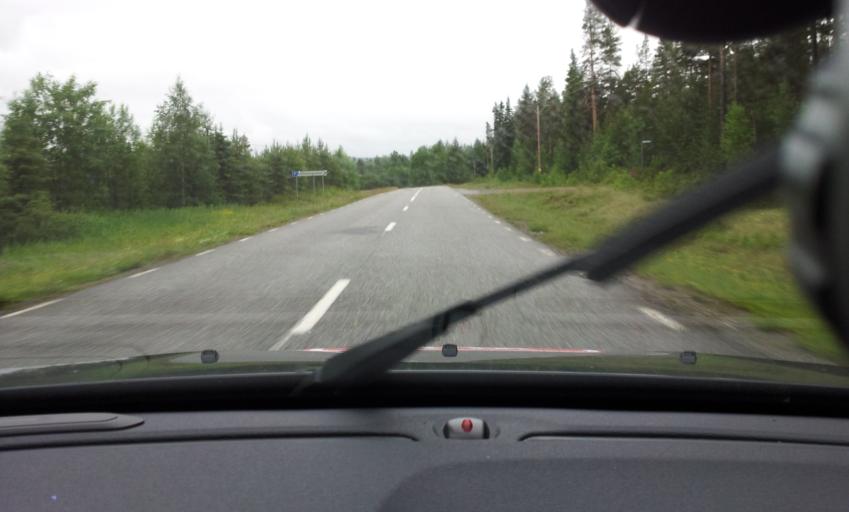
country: SE
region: Jaemtland
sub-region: Stroemsunds Kommun
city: Stroemsund
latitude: 63.3070
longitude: 15.7598
